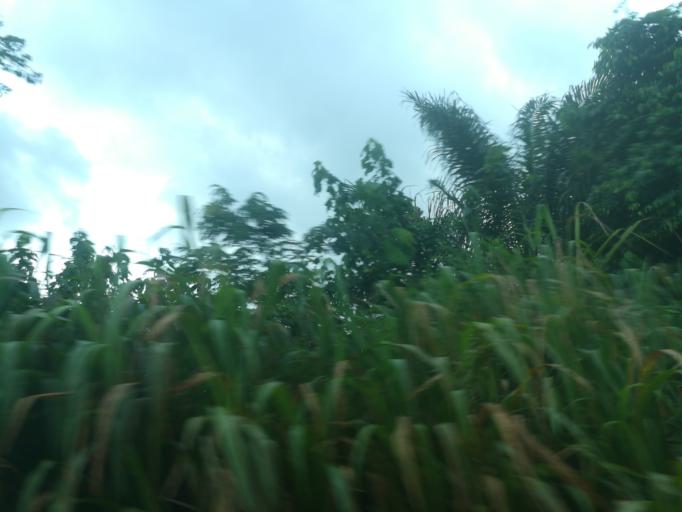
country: NG
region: Lagos
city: Ikorodu
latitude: 6.6638
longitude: 3.5998
